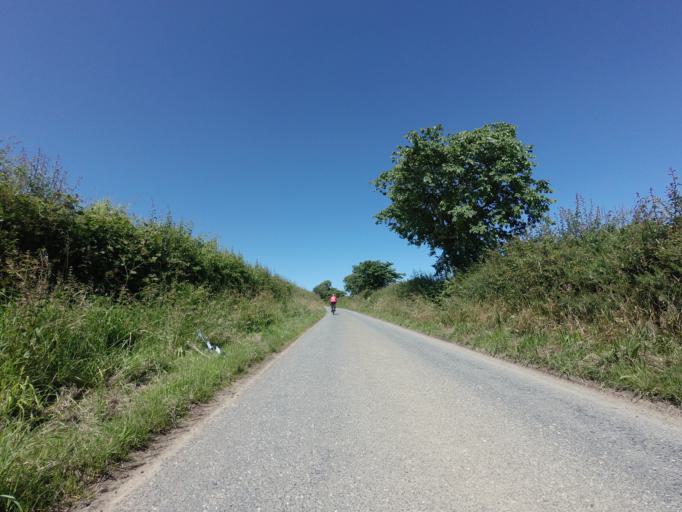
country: GB
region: Scotland
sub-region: Aberdeenshire
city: Macduff
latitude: 57.6358
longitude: -2.4914
